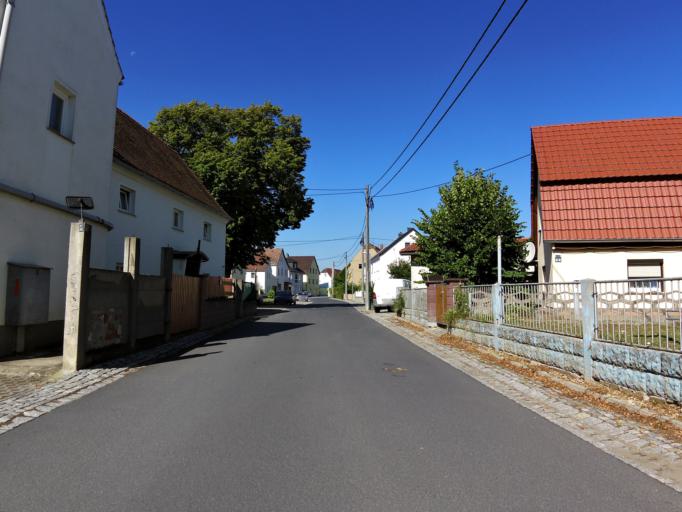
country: DE
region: Saxony
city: Riesa
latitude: 51.3434
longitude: 13.2902
